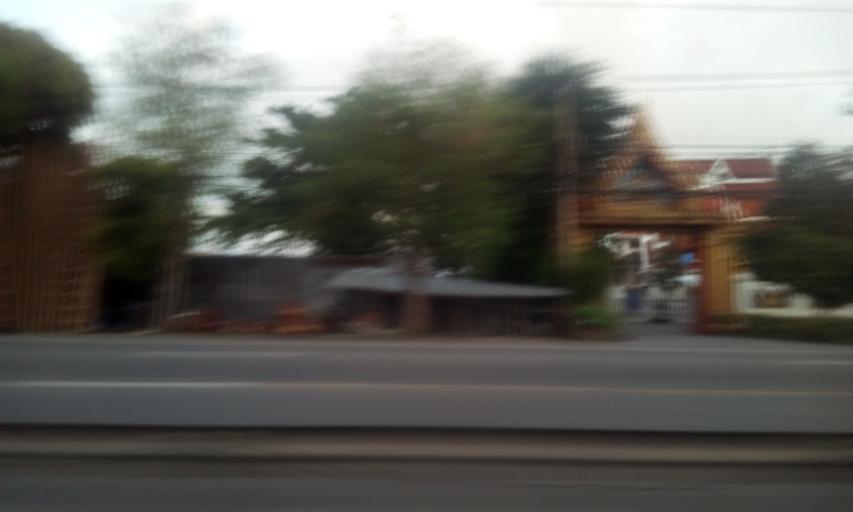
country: TH
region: Pathum Thani
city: Thanyaburi
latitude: 13.9977
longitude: 100.6762
